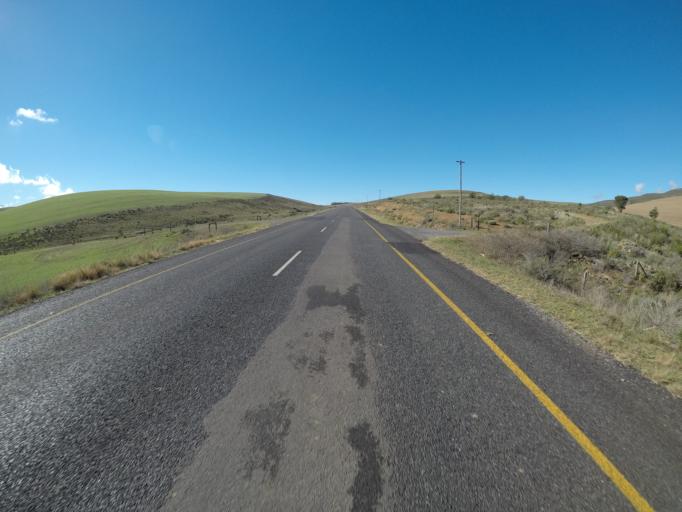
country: ZA
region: Western Cape
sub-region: Overberg District Municipality
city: Caledon
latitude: -34.1483
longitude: 19.4858
